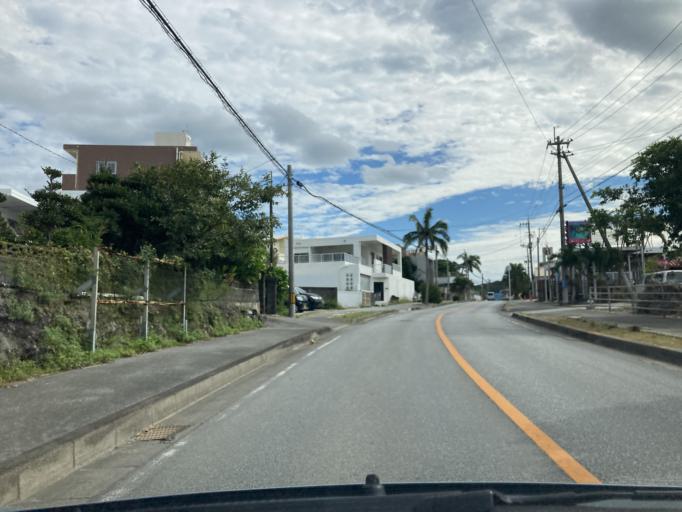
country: JP
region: Okinawa
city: Ishikawa
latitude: 26.4389
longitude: 127.7733
